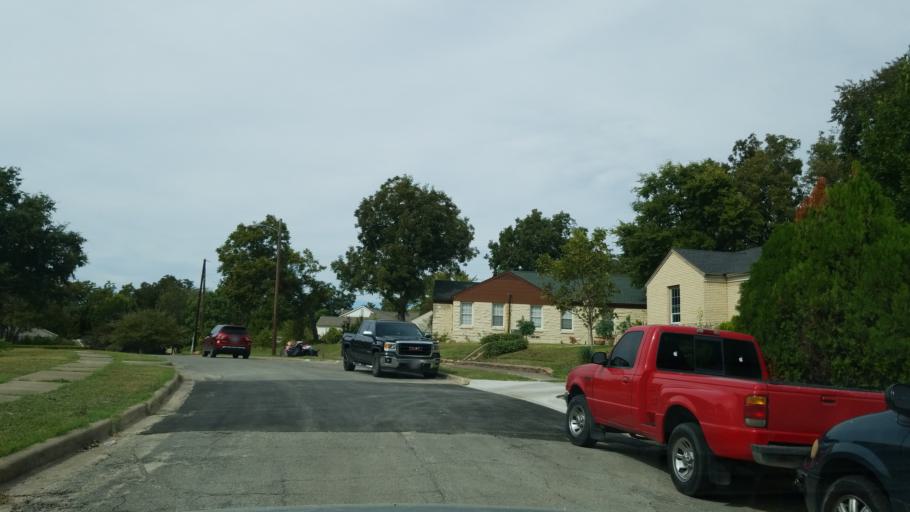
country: US
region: Texas
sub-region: Dallas County
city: Dallas
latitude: 32.7706
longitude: -96.7197
